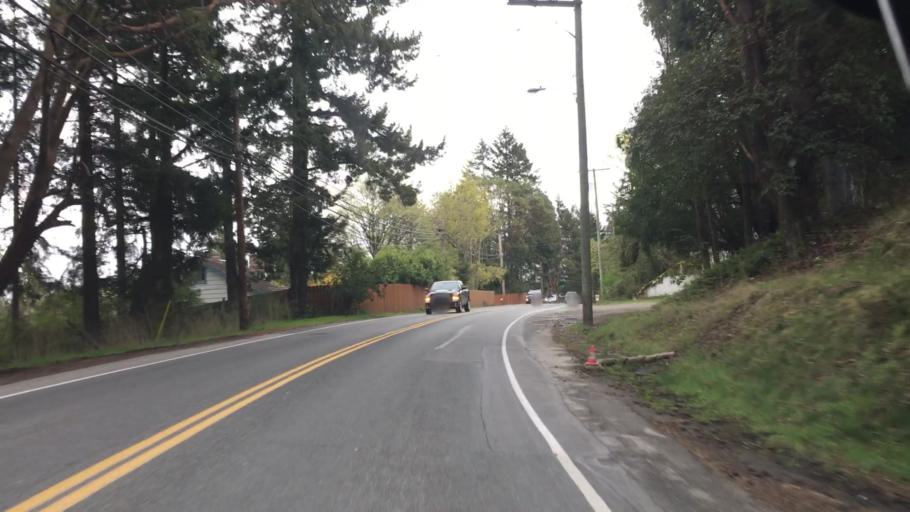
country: CA
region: British Columbia
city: North Saanich
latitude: 48.5660
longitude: -123.4240
